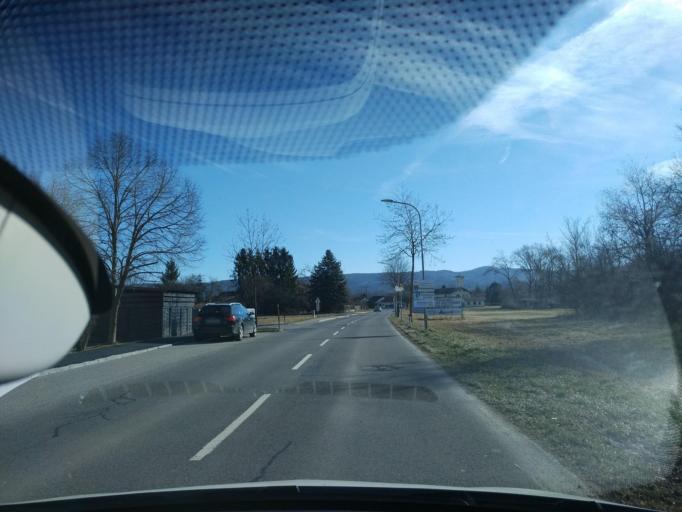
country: AT
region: Lower Austria
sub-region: Politischer Bezirk Wiener Neustadt
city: Bad Erlach
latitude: 47.7371
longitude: 16.2186
